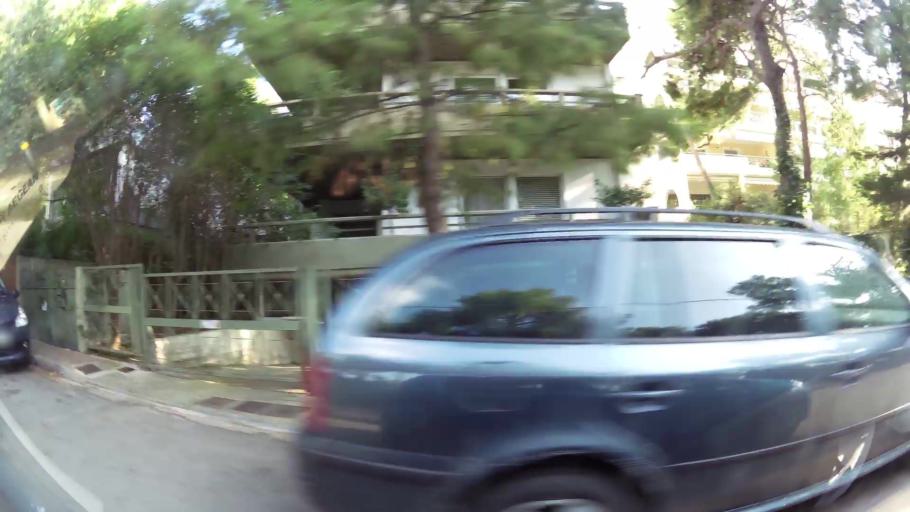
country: GR
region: Attica
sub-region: Nomarchia Athinas
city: Agia Paraskevi
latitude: 38.0118
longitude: 23.8270
